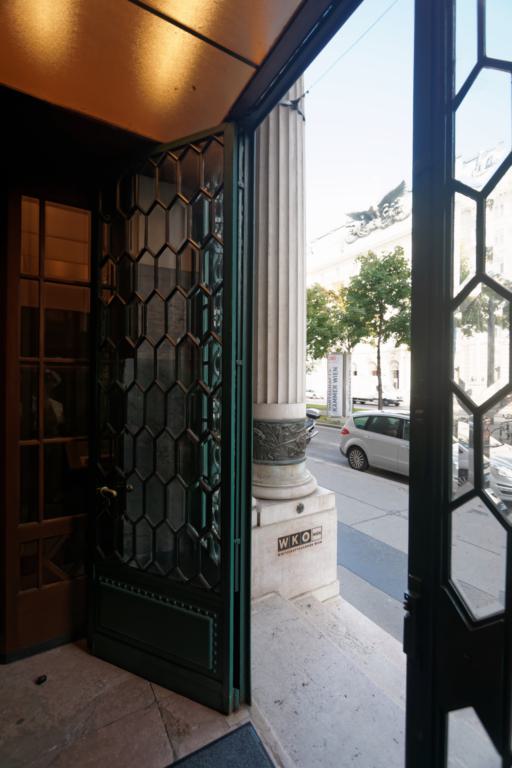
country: AT
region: Vienna
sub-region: Wien Stadt
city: Vienna
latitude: 48.2096
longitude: 16.3821
